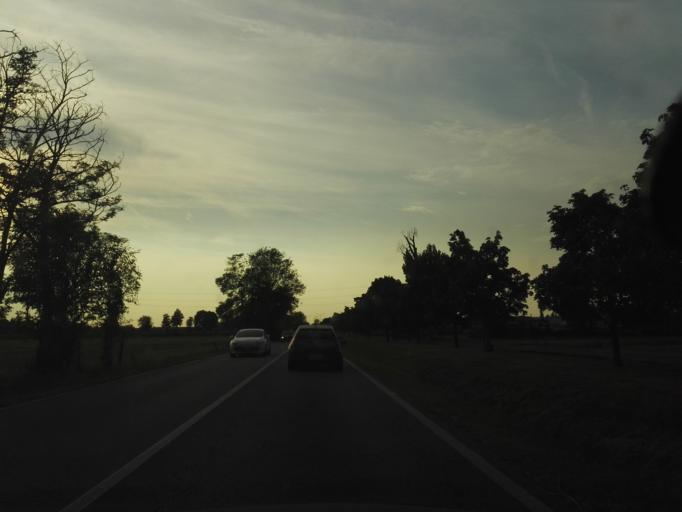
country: IT
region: Lombardy
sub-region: Citta metropolitana di Milano
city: Bettola-Zeloforomagno
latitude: 45.4340
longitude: 9.3041
